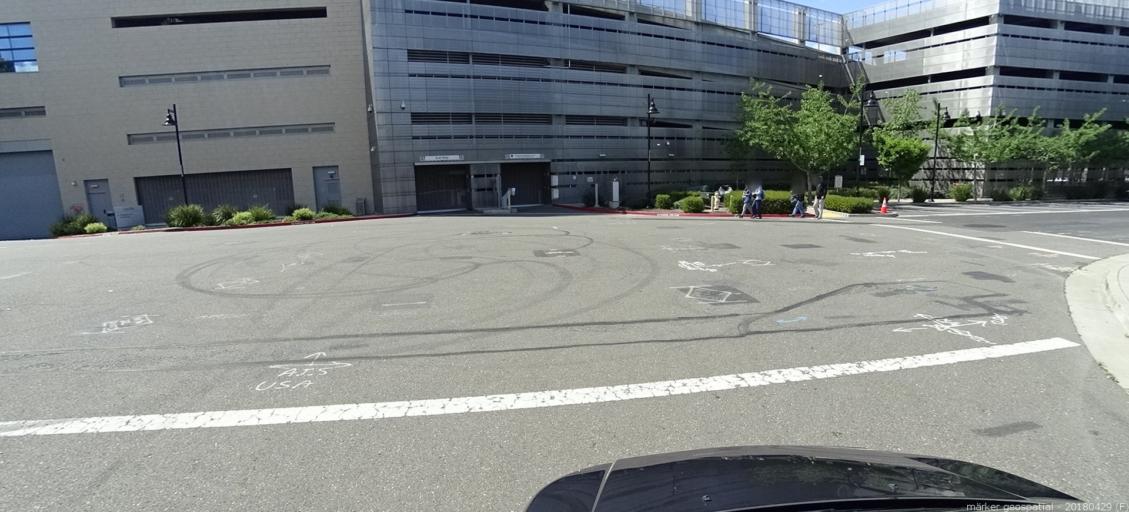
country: US
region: California
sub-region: Sacramento County
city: Sacramento
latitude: 38.5858
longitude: -121.5092
